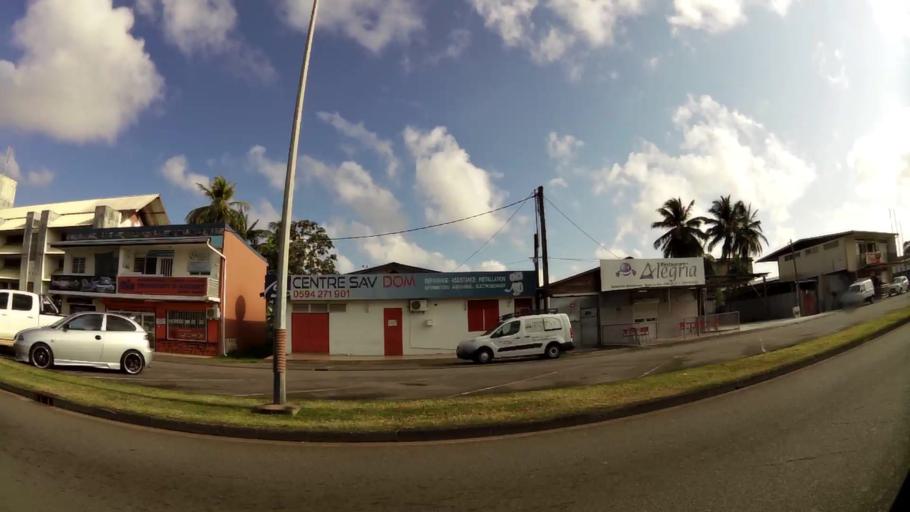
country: GF
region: Guyane
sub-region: Guyane
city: Cayenne
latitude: 4.9376
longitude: -52.3250
